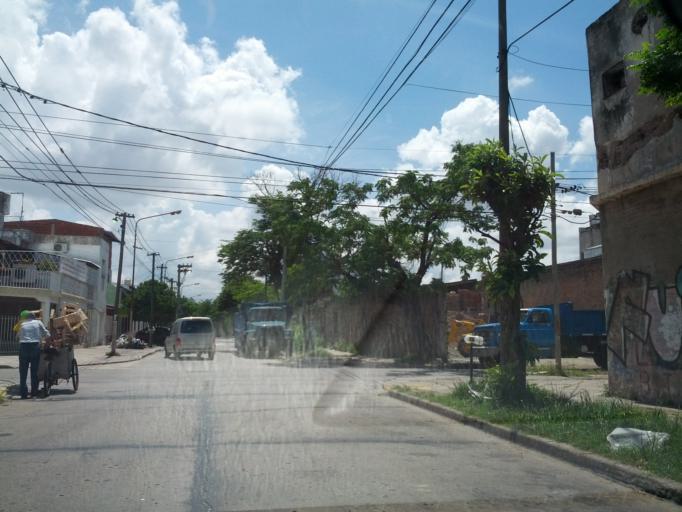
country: AR
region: Buenos Aires
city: San Justo
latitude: -34.6475
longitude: -58.5502
